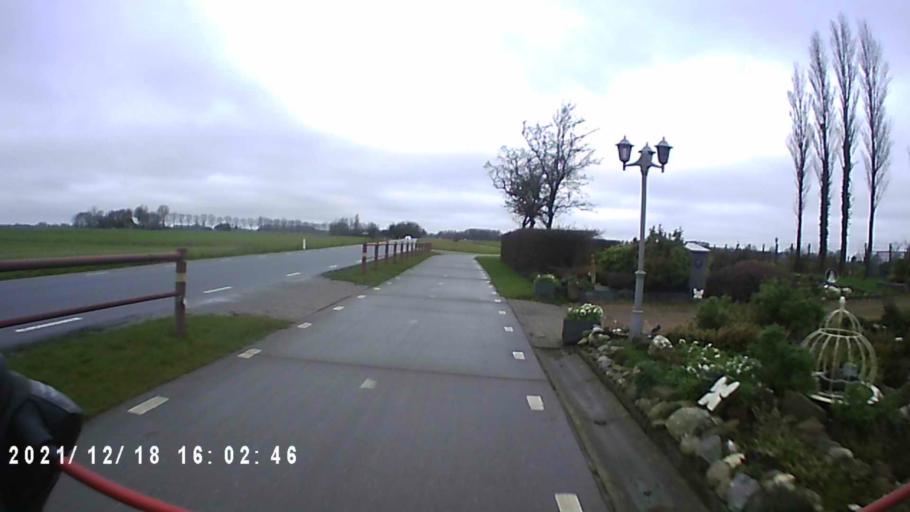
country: NL
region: Friesland
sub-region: Gemeente Dongeradeel
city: Anjum
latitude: 53.3482
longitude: 6.0827
